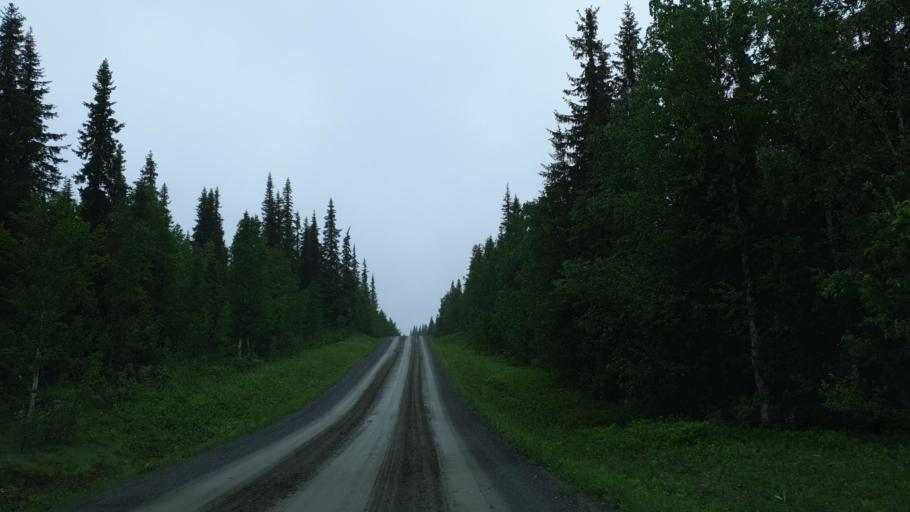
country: SE
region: Vaesterbotten
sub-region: Vilhelmina Kommun
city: Sjoberg
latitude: 65.2645
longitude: 15.9396
